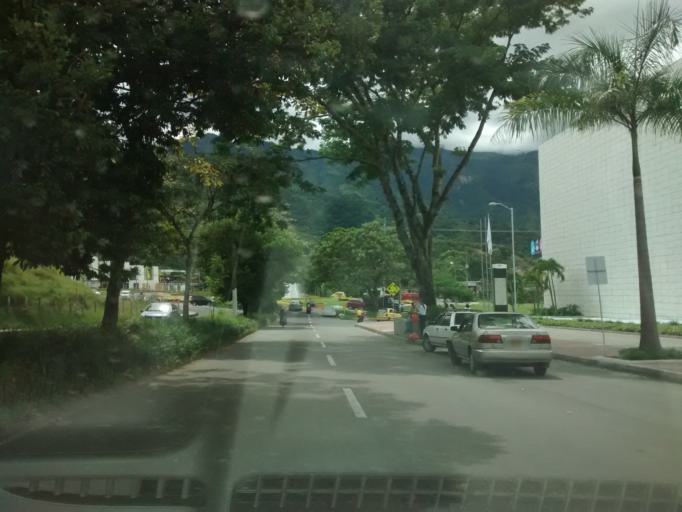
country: CO
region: Tolima
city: Ibague
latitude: 4.4458
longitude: -75.2058
